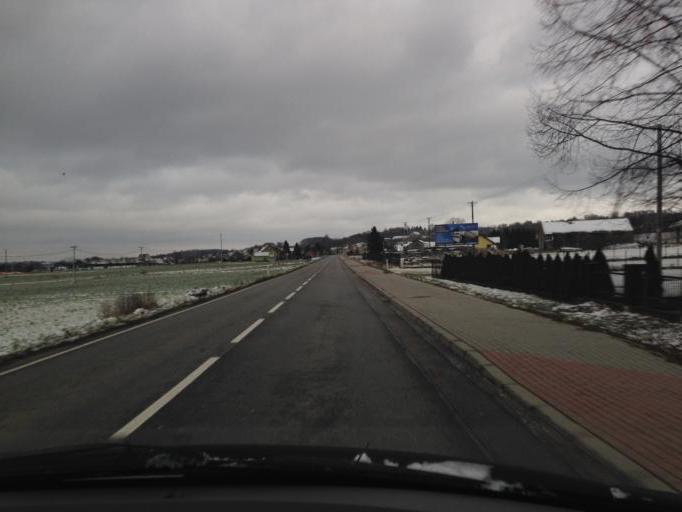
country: PL
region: Lesser Poland Voivodeship
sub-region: Powiat tarnowski
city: Zakliczyn
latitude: 49.8518
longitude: 20.8321
